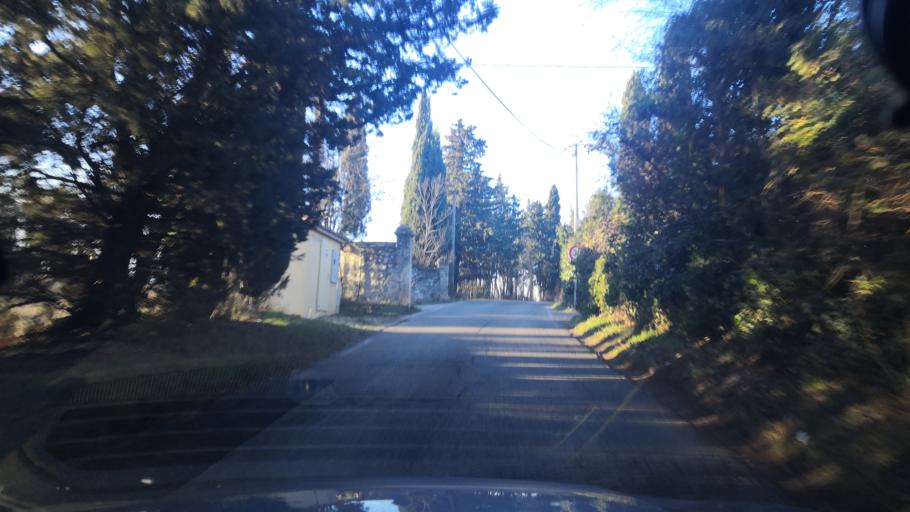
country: FR
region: Provence-Alpes-Cote d'Azur
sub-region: Departement des Bouches-du-Rhone
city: Aix-en-Provence
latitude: 43.5176
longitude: 5.4155
